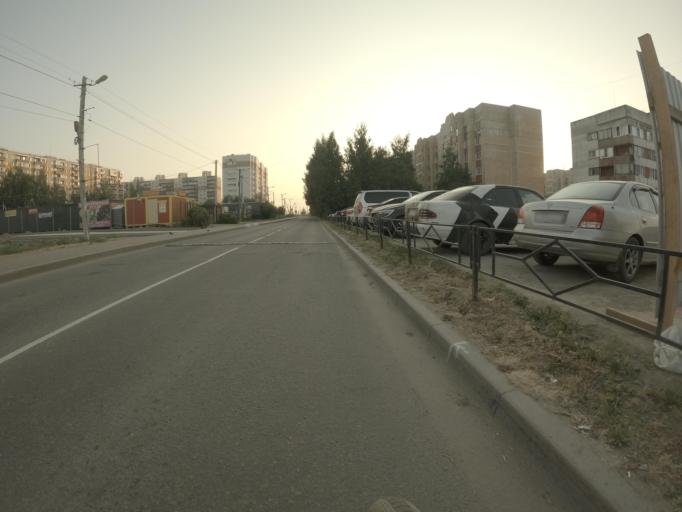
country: RU
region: St.-Petersburg
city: Pontonnyy
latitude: 59.7982
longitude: 30.6361
